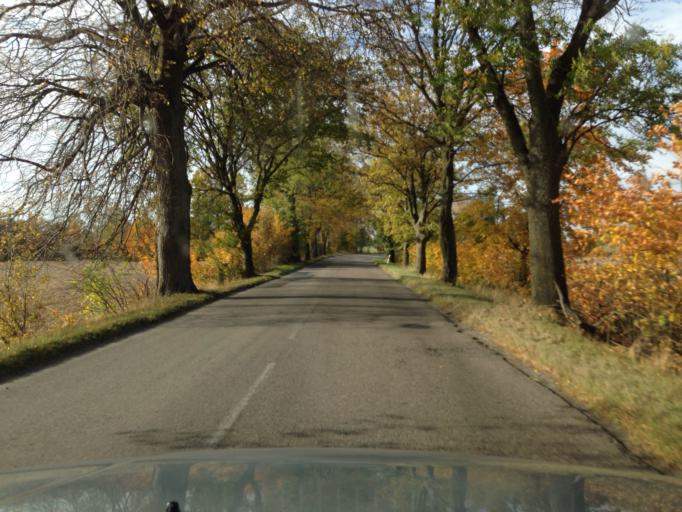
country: PL
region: Pomeranian Voivodeship
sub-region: Powiat koscierski
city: Stara Kiszewa
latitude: 54.0232
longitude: 18.0964
